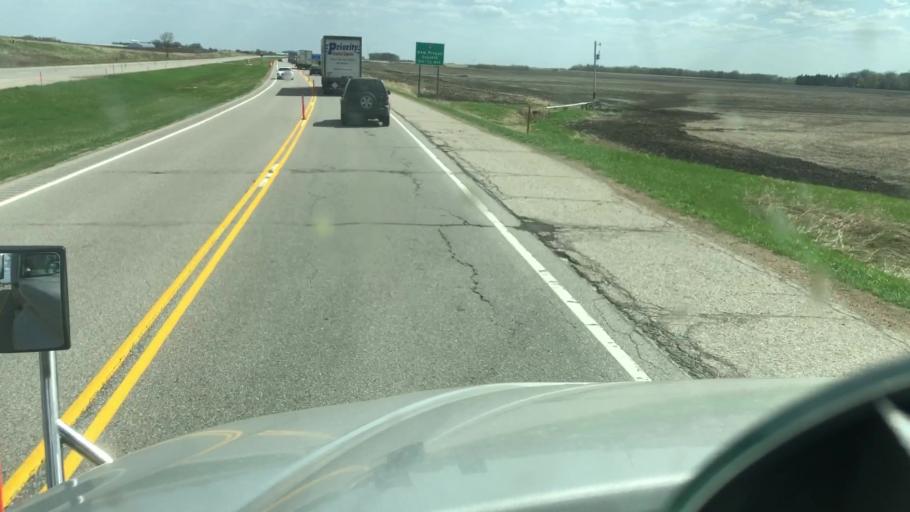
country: US
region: Minnesota
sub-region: Scott County
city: Belle Plaine
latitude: 44.5568
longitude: -93.8511
